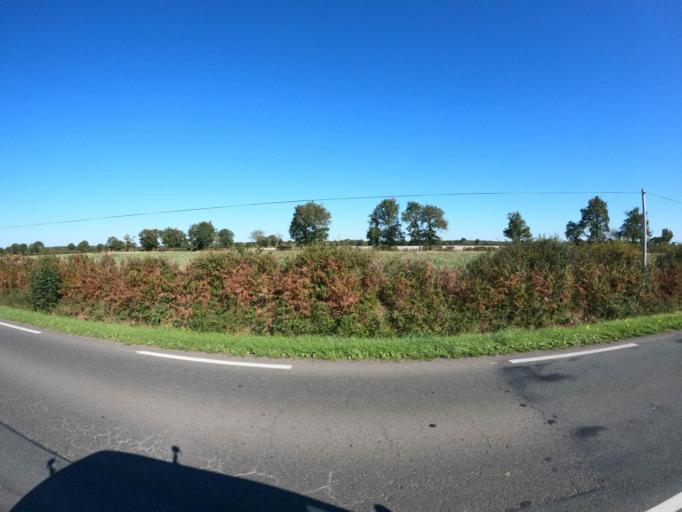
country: FR
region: Poitou-Charentes
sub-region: Departement des Deux-Sevres
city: Thenezay
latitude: 46.6578
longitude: -0.0474
